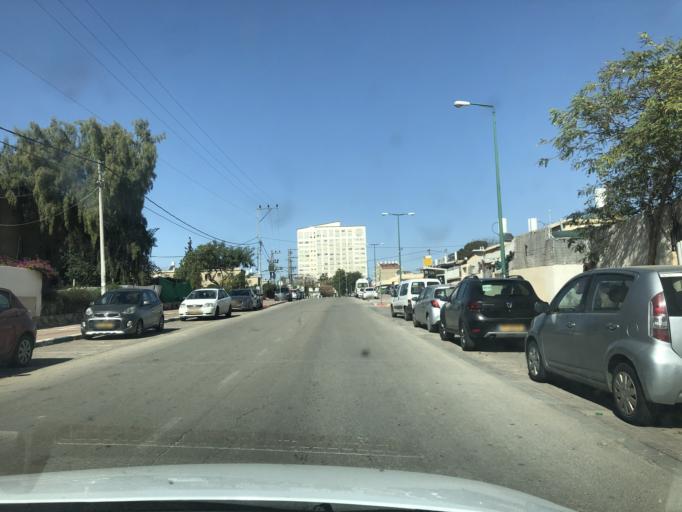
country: IL
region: Southern District
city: Beersheba
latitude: 31.2602
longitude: 34.7950
